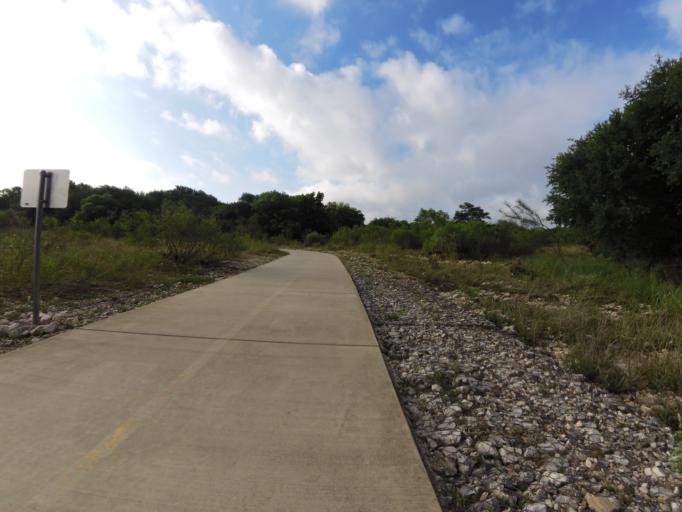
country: US
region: Texas
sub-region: Bexar County
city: Leon Valley
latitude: 29.4761
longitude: -98.6368
